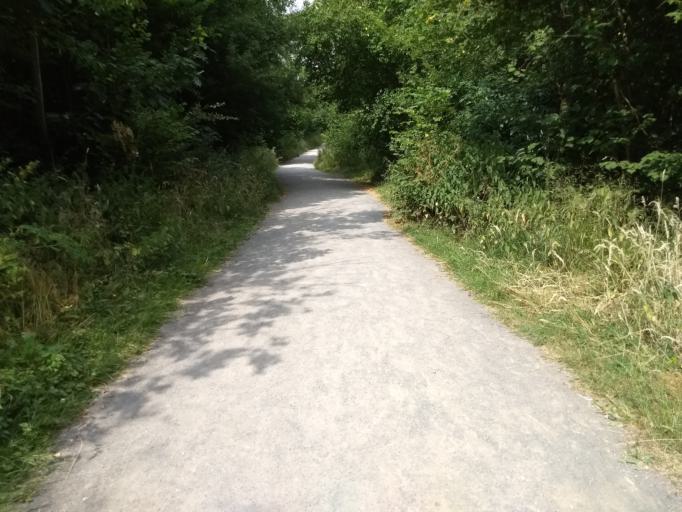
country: GB
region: England
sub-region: Northamptonshire
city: Hartwell
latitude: 52.1588
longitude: -0.8387
